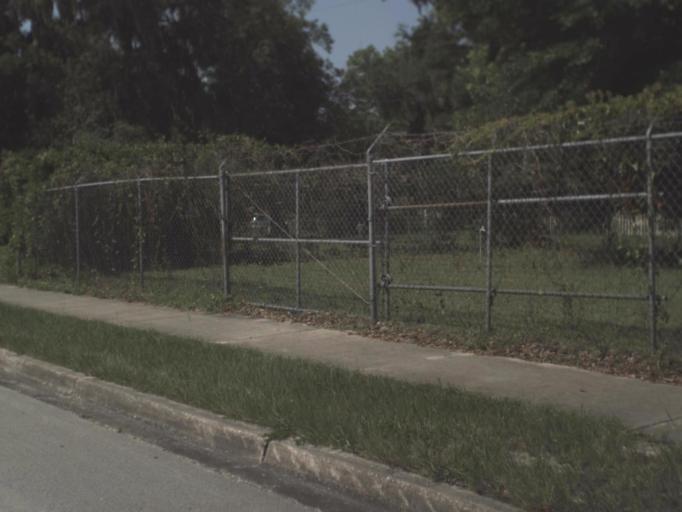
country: US
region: Florida
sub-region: Alachua County
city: Hawthorne
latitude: 29.5942
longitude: -82.0855
